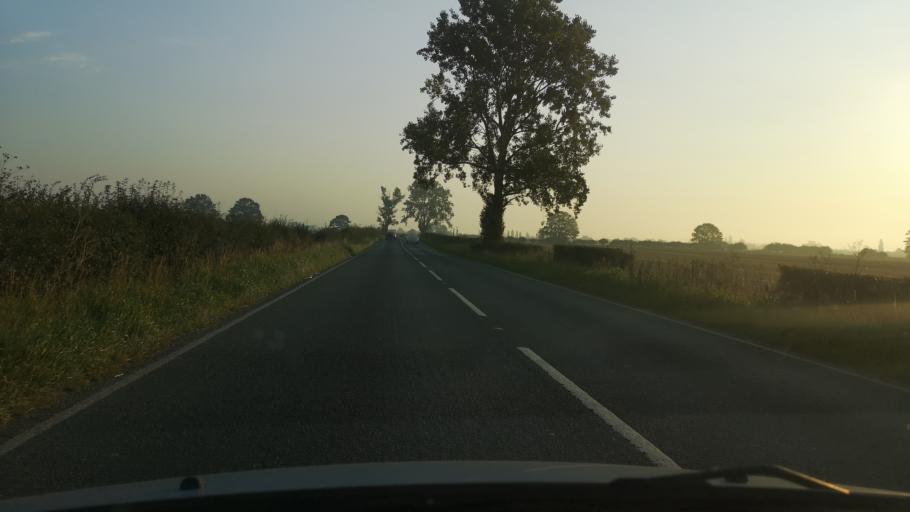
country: GB
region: England
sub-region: Doncaster
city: Stainforth
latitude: 53.5916
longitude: -1.0497
